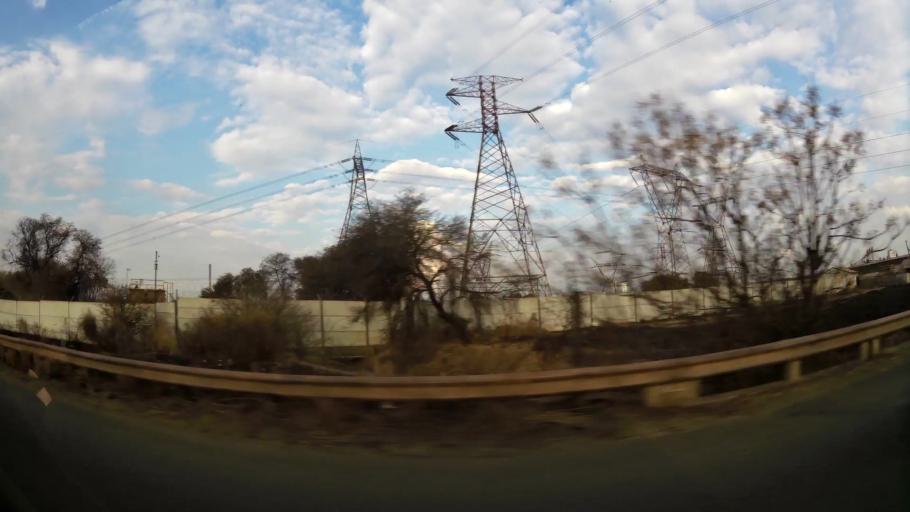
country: ZA
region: Gauteng
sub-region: Sedibeng District Municipality
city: Vanderbijlpark
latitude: -26.6638
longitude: 27.7975
